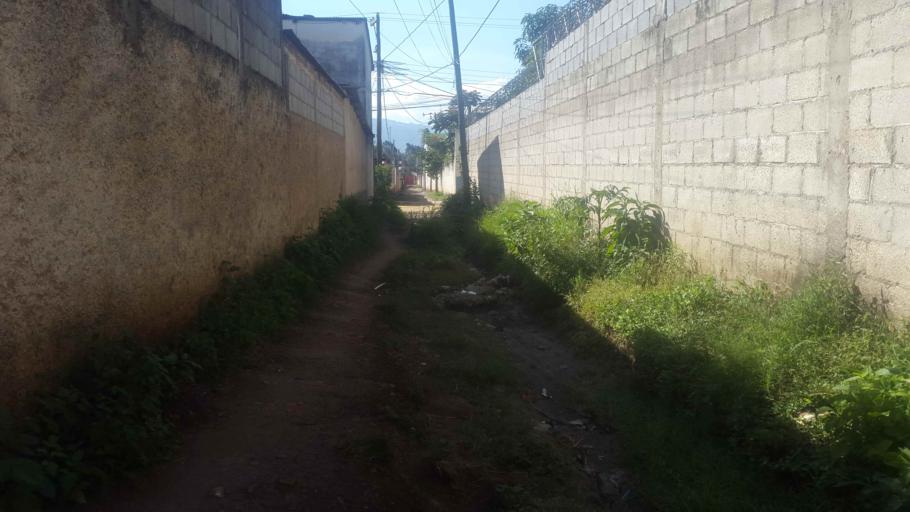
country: GT
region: Guatemala
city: Petapa
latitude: 14.5134
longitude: -90.5409
